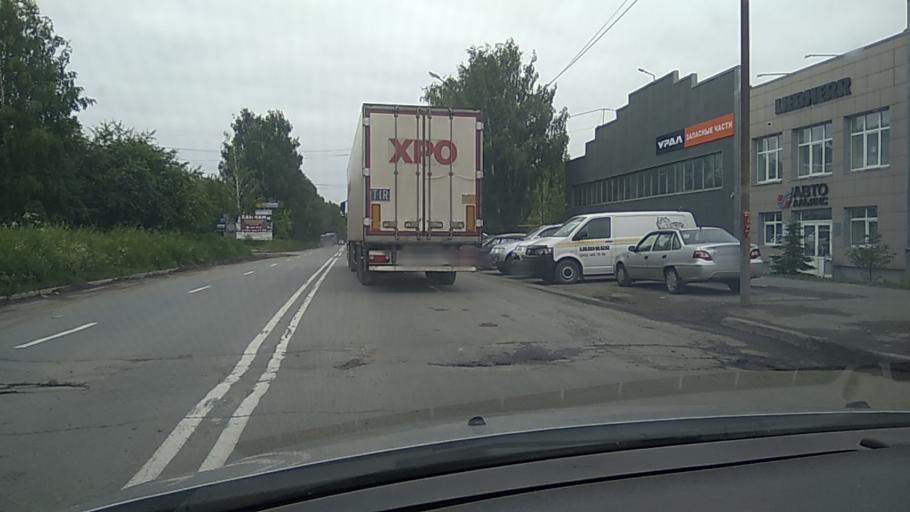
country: RU
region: Sverdlovsk
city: Shuvakish
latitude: 56.8903
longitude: 60.5206
